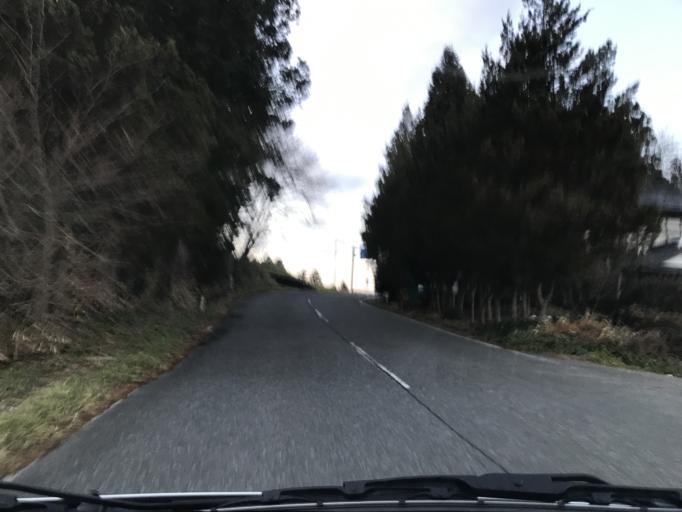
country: JP
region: Iwate
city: Ichinoseki
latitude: 38.8384
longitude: 141.1288
